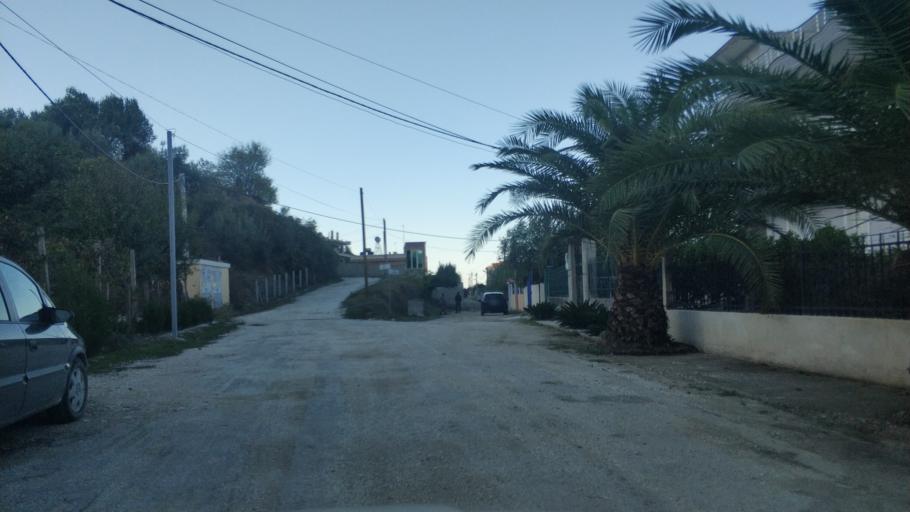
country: AL
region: Vlore
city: Vlore
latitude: 40.5132
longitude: 19.4196
